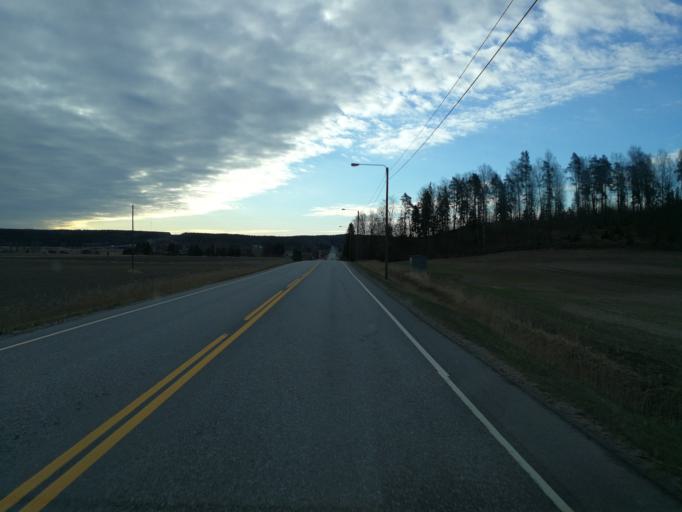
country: FI
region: Varsinais-Suomi
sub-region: Turku
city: Paimio
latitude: 60.4238
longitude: 22.6400
